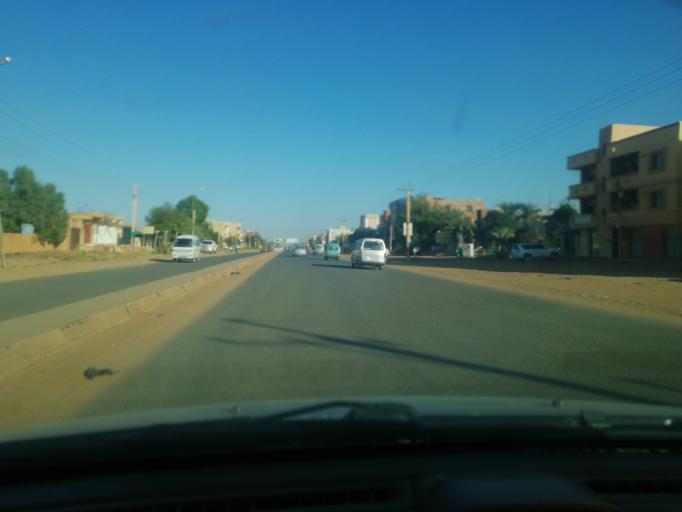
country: SD
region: Khartoum
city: Khartoum
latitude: 15.6101
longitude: 32.6220
